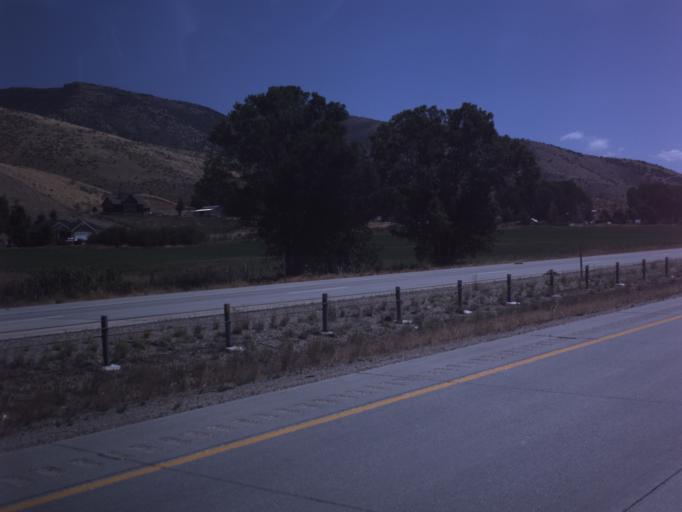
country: US
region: Utah
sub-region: Morgan County
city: Morgan
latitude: 41.0617
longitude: -111.7047
